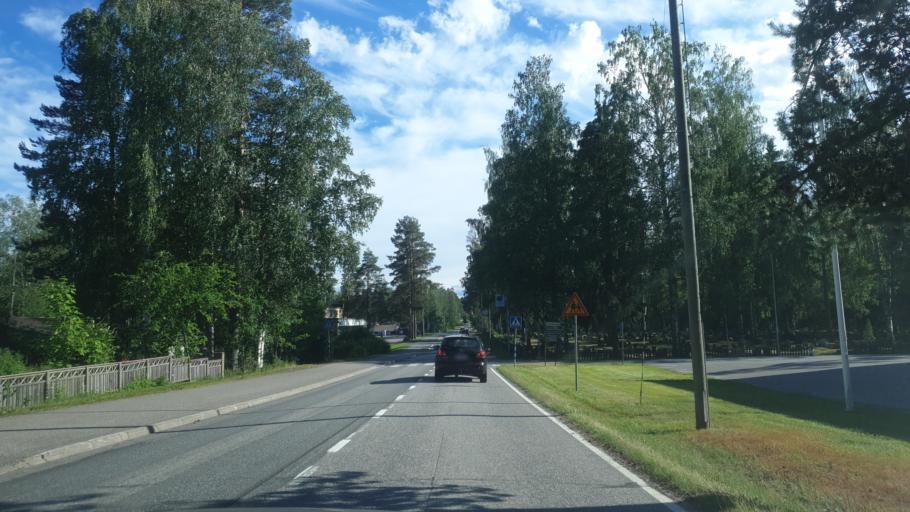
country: FI
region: Southern Savonia
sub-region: Mikkeli
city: Pertunmaa
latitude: 61.5076
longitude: 26.4823
